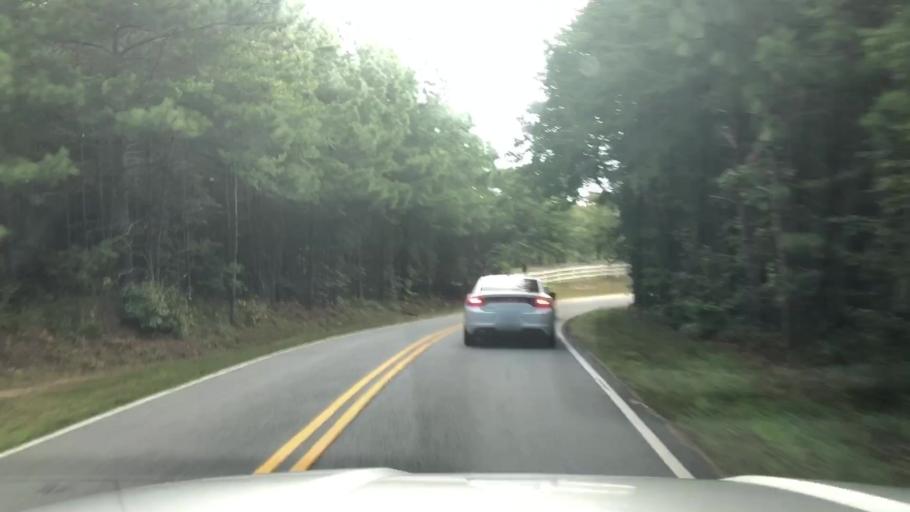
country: US
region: Georgia
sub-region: Bartow County
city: Euharlee
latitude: 34.0479
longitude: -84.8634
